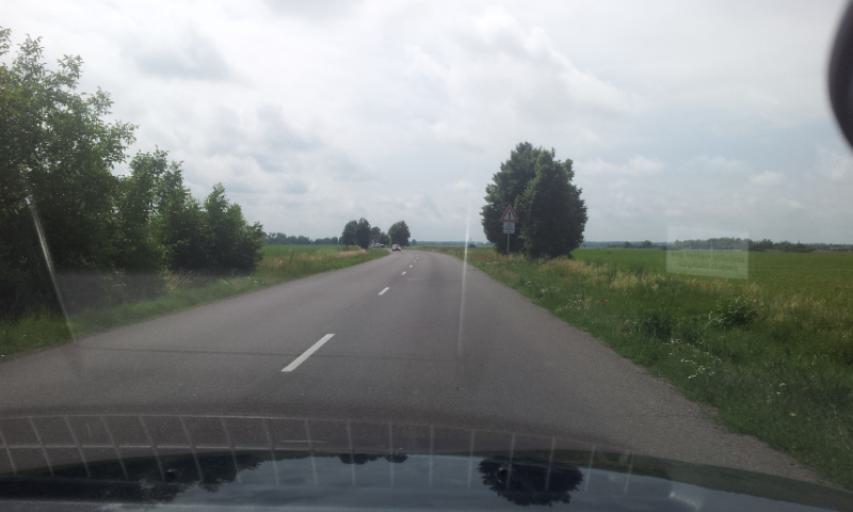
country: SK
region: Kosicky
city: Michalovce
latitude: 48.7324
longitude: 21.9540
